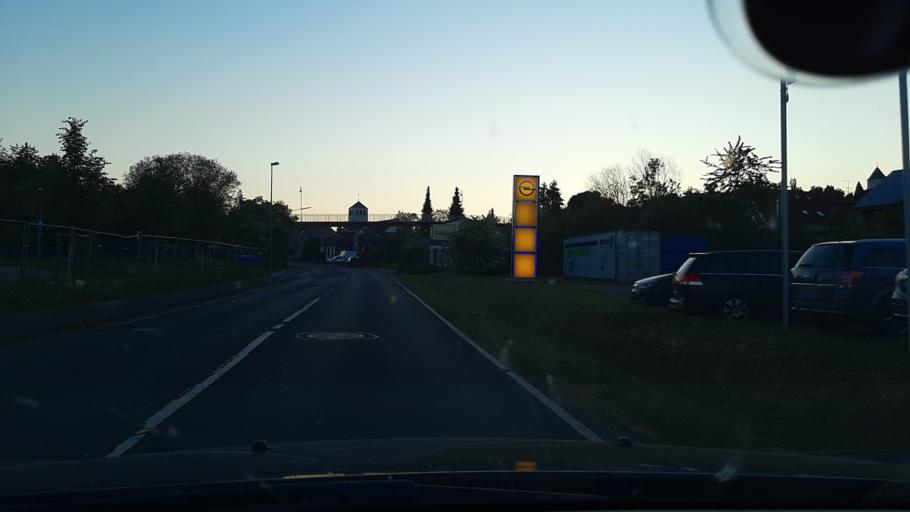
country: DE
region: North Rhine-Westphalia
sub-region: Regierungsbezirk Koln
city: Mechernich
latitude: 50.5919
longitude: 6.6604
